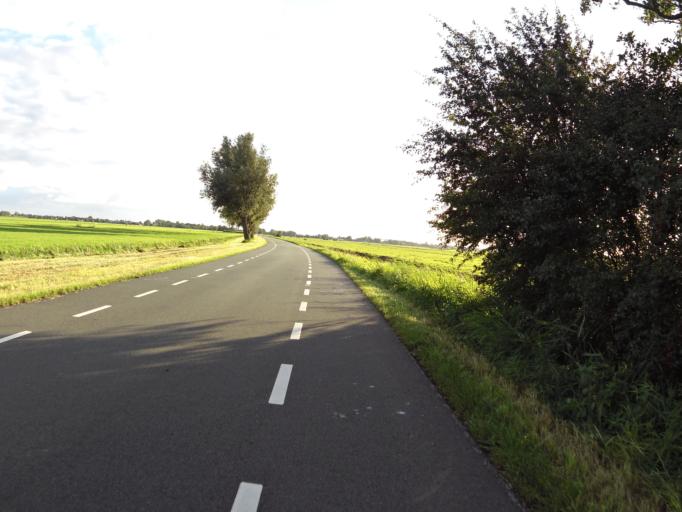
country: NL
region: South Holland
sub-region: Gemeente Alphen aan den Rijn
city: Alphen aan den Rijn
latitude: 52.1296
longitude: 4.7018
